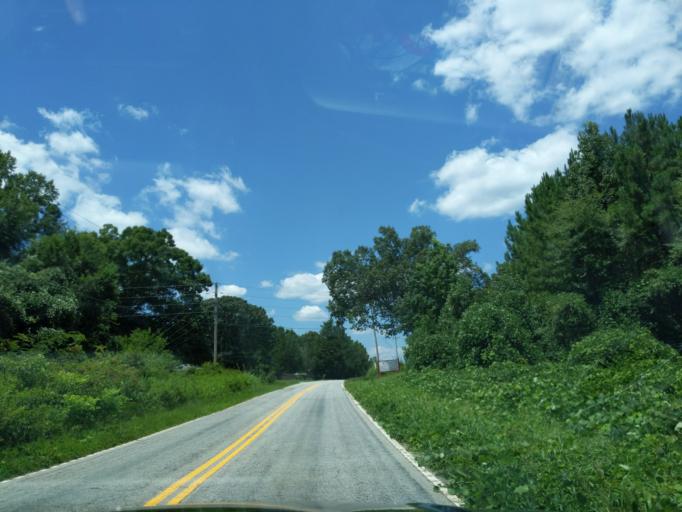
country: US
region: South Carolina
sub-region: Laurens County
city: Clinton
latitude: 34.5258
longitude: -81.9094
